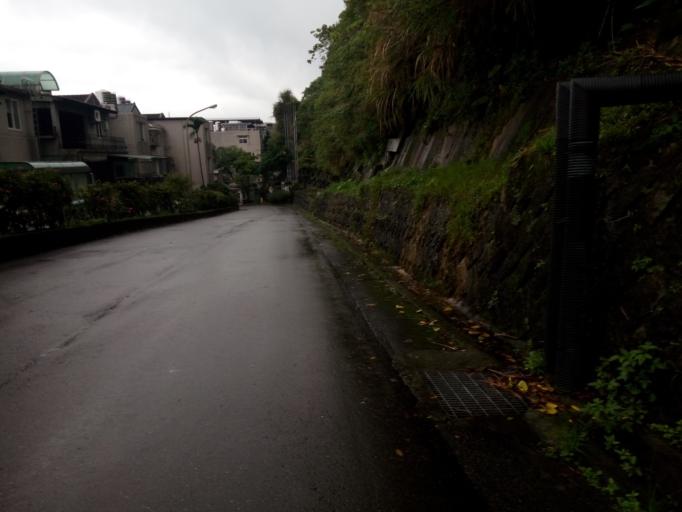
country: TW
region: Taiwan
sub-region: Keelung
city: Keelung
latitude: 25.0558
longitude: 121.6670
